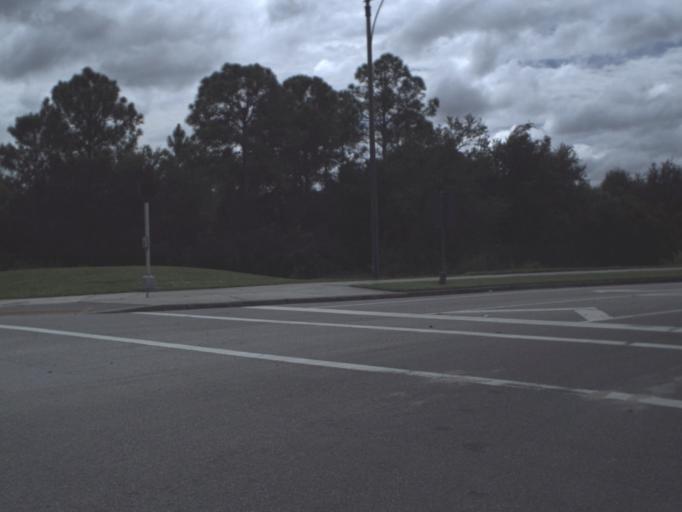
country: US
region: Florida
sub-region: Sarasota County
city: Warm Mineral Springs
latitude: 27.0612
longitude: -82.3162
